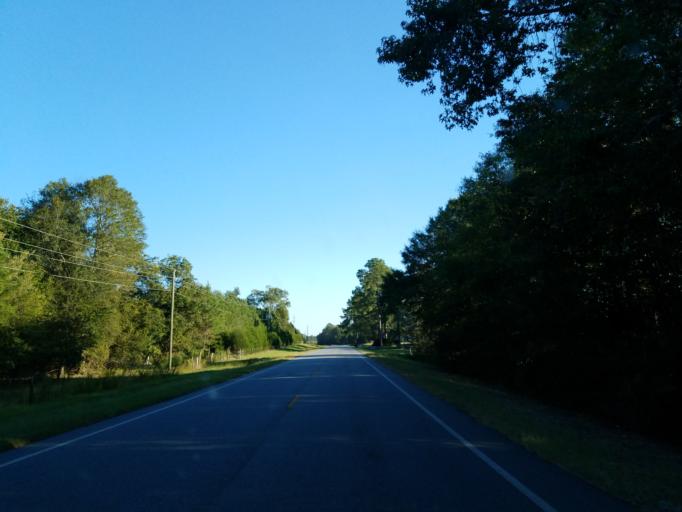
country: US
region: Georgia
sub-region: Worth County
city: Sylvester
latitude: 31.6948
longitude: -83.8847
